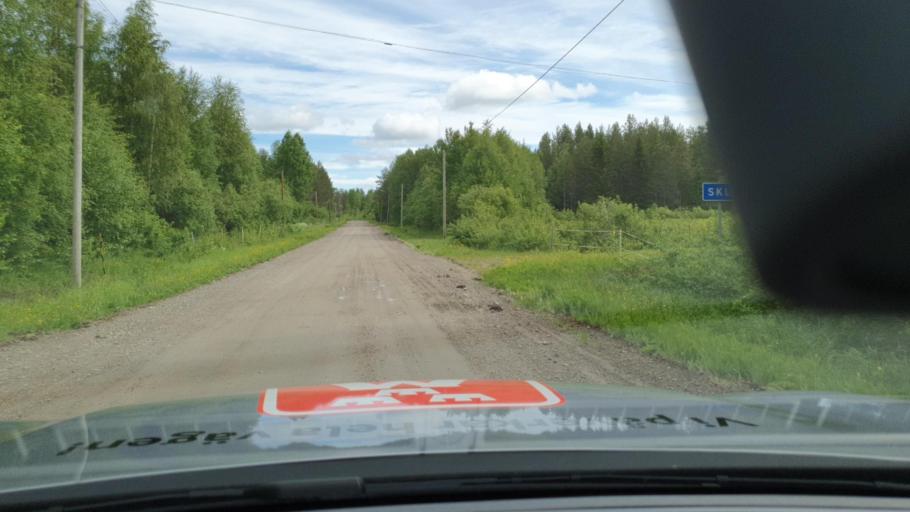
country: SE
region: Norrbotten
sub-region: Kalix Kommun
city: Rolfs
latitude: 65.8894
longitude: 23.0906
